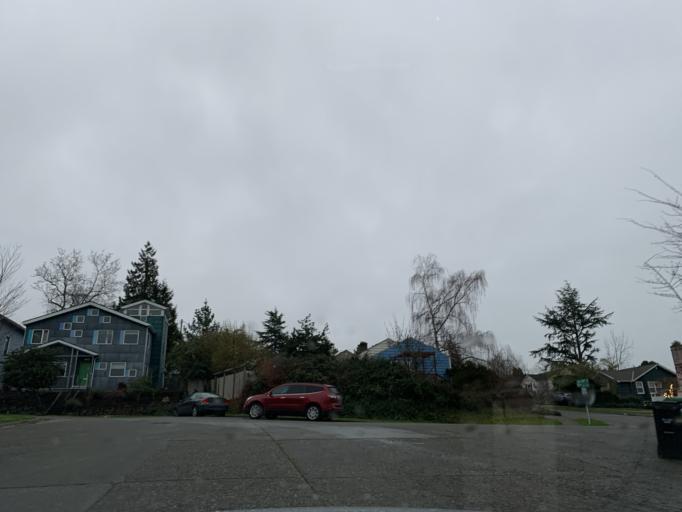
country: US
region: Washington
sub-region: King County
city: Yarrow Point
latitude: 47.6703
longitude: -122.2673
